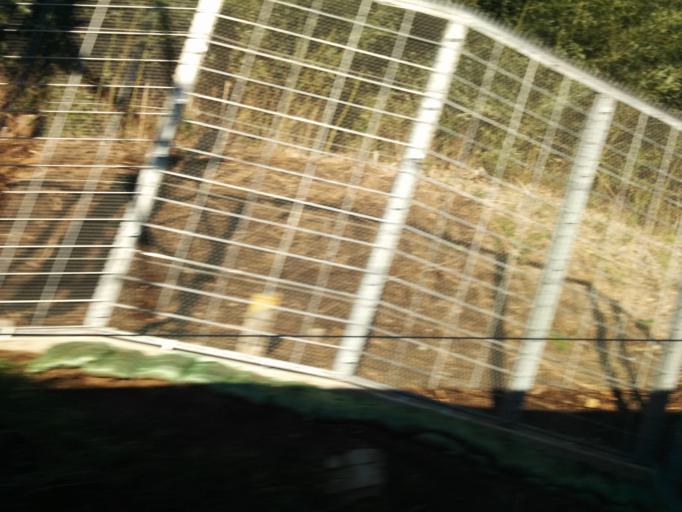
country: JP
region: Kanagawa
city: Yokohama
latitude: 35.4912
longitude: 139.5981
